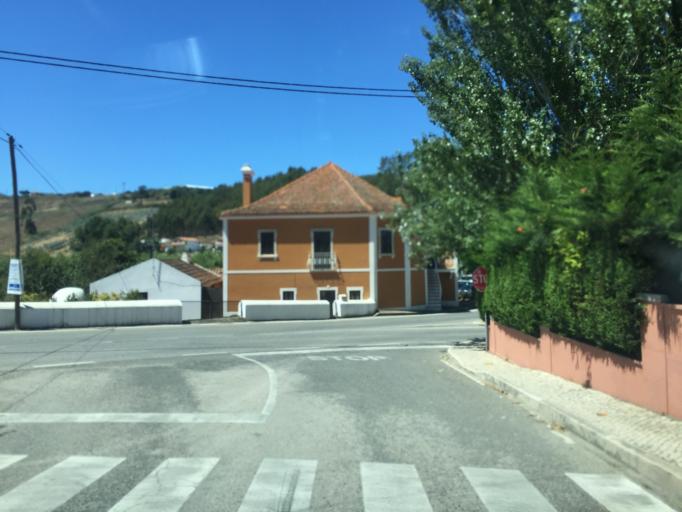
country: PT
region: Lisbon
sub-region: Torres Vedras
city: A dos Cunhados
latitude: 39.1767
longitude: -9.3207
